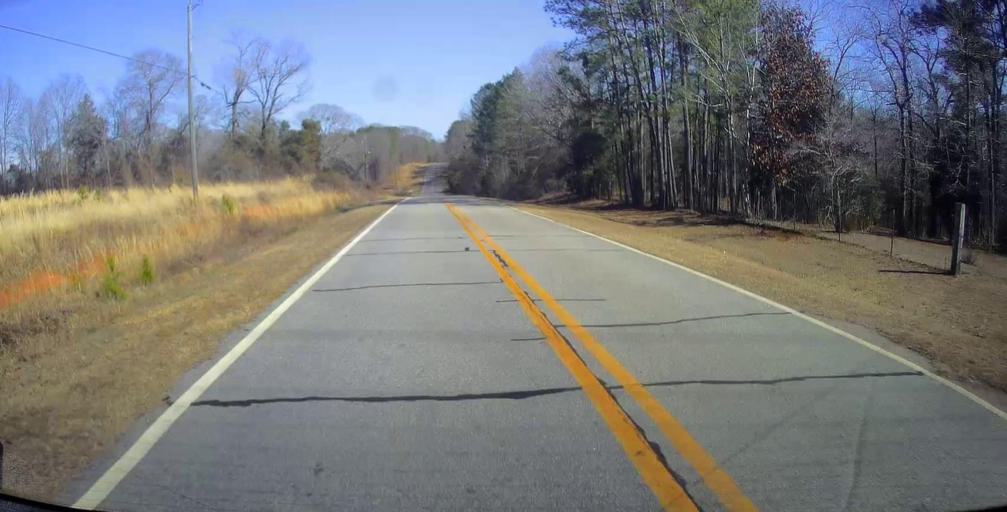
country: US
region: Georgia
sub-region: Peach County
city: Byron
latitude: 32.6111
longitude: -83.8152
